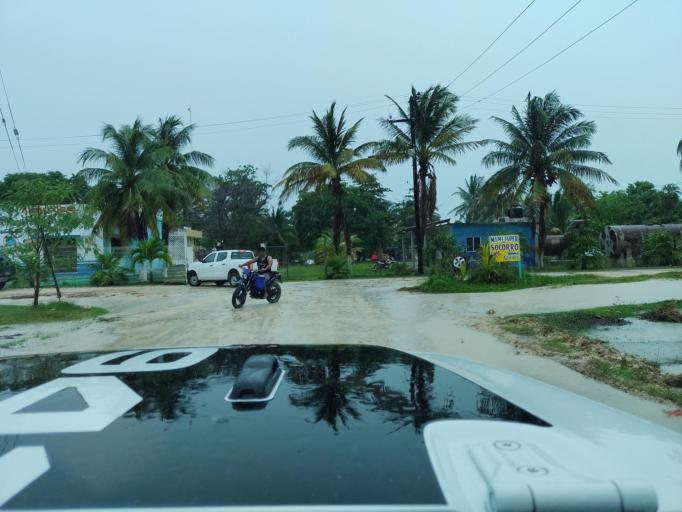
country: MX
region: Quintana Roo
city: Tulum
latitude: 19.8006
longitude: -87.4771
